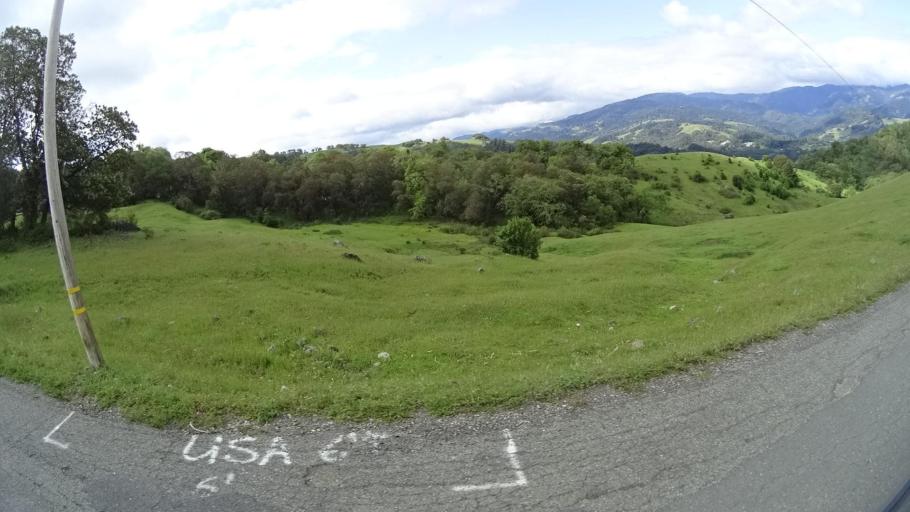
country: US
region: California
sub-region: Humboldt County
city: Redway
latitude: 40.1835
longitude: -123.5738
